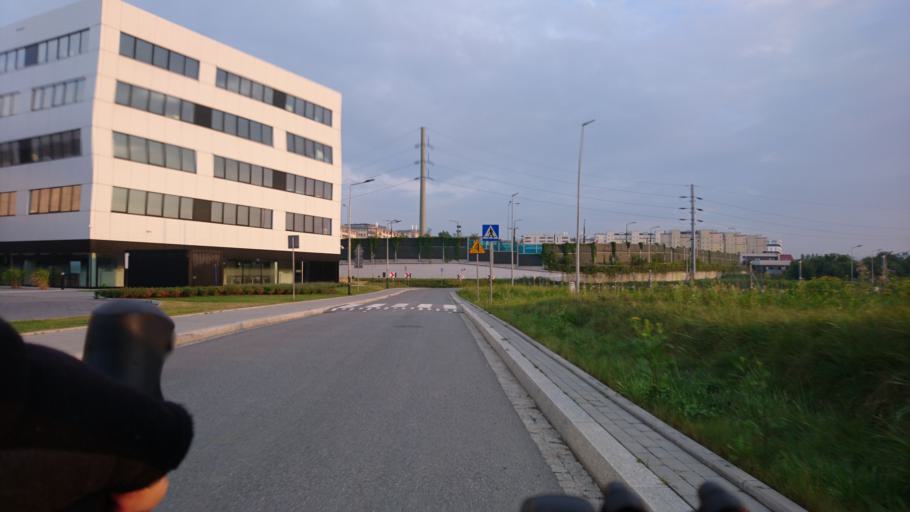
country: PL
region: Lesser Poland Voivodeship
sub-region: Krakow
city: Sidzina
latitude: 50.0198
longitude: 19.8890
